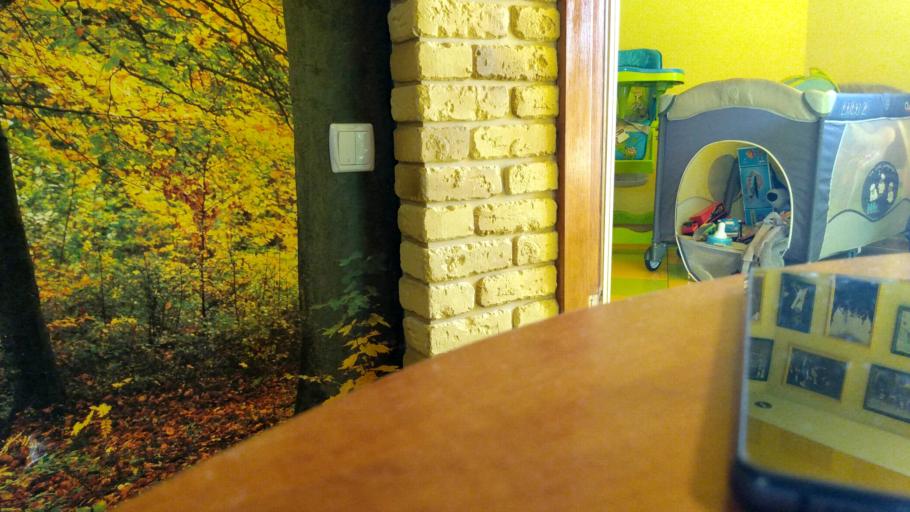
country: RU
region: Tverskaya
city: Likhoslavl'
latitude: 57.2294
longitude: 35.4656
